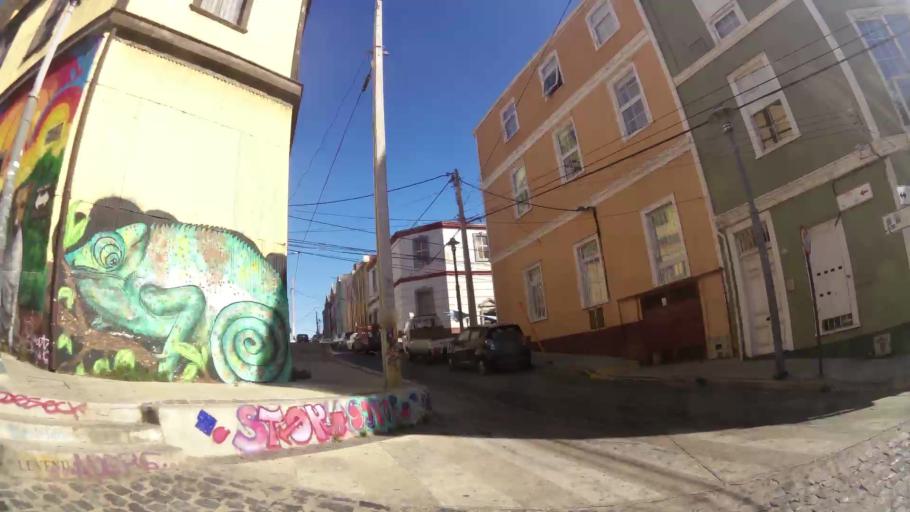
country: CL
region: Valparaiso
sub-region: Provincia de Valparaiso
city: Valparaiso
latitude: -33.0441
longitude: -71.6301
